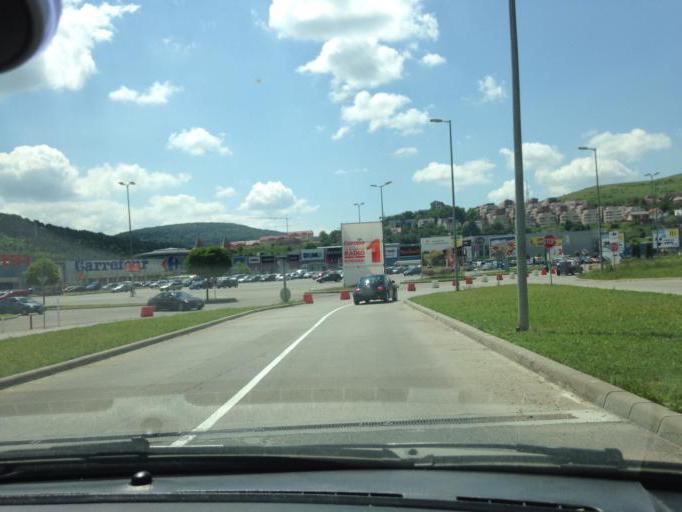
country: RO
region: Cluj
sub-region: Comuna Floresti
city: Floresti
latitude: 46.7522
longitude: 23.5310
